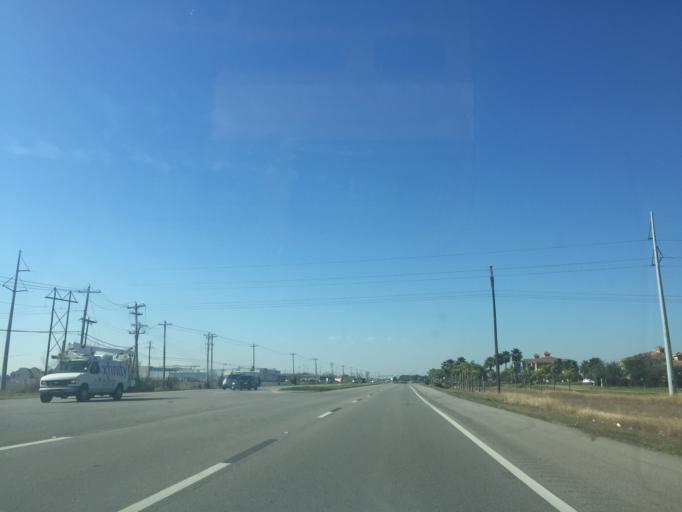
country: US
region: Texas
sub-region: Galveston County
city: Kemah
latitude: 29.5093
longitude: -95.0363
